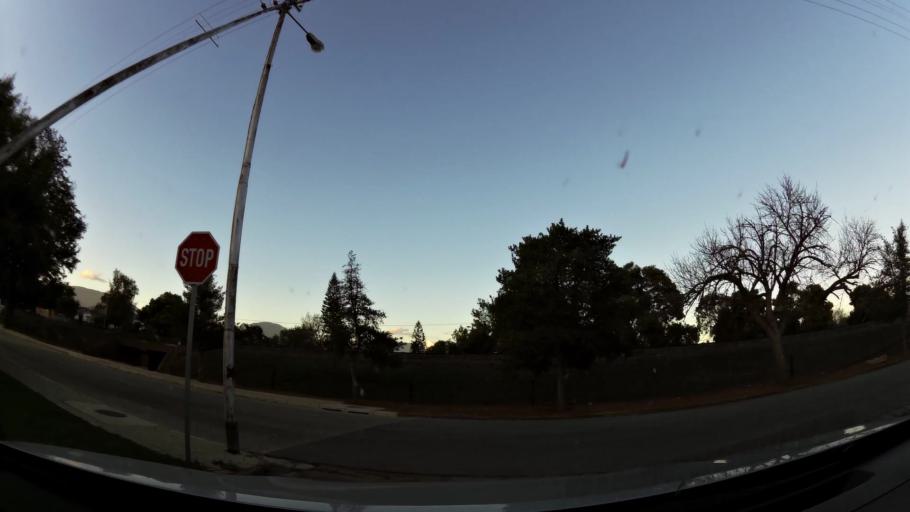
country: ZA
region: Western Cape
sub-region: Eden District Municipality
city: Riversdale
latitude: -34.0900
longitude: 21.2541
